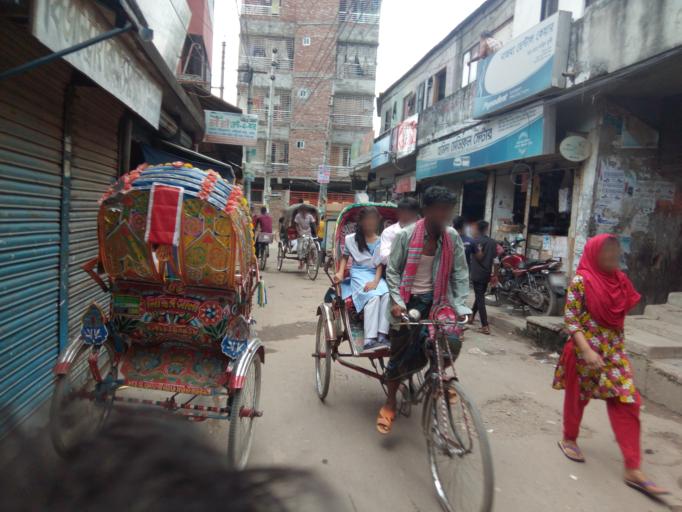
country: BD
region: Dhaka
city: Paltan
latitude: 23.7568
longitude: 90.4141
